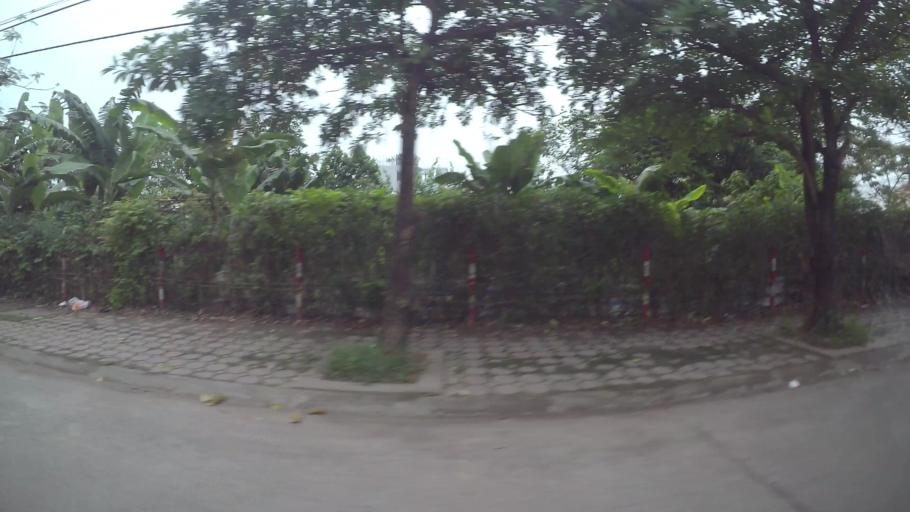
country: VN
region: Ha Noi
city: Hai BaTrung
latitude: 20.9953
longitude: 105.8830
